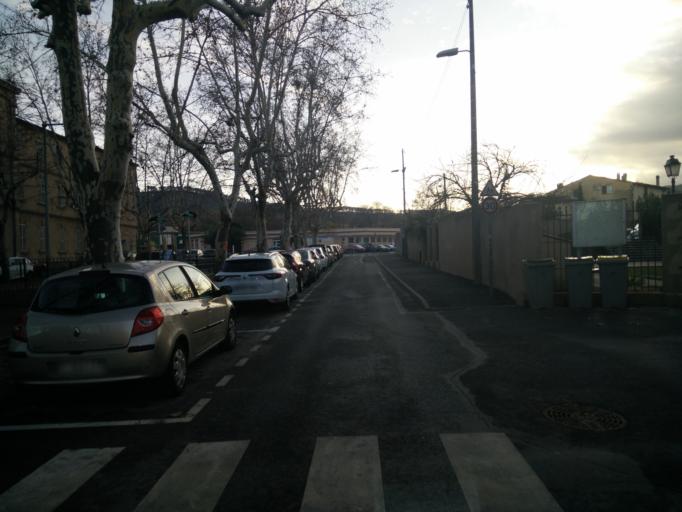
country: FR
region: Provence-Alpes-Cote d'Azur
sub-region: Departement du Var
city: Brignoles
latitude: 43.4049
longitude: 6.0647
